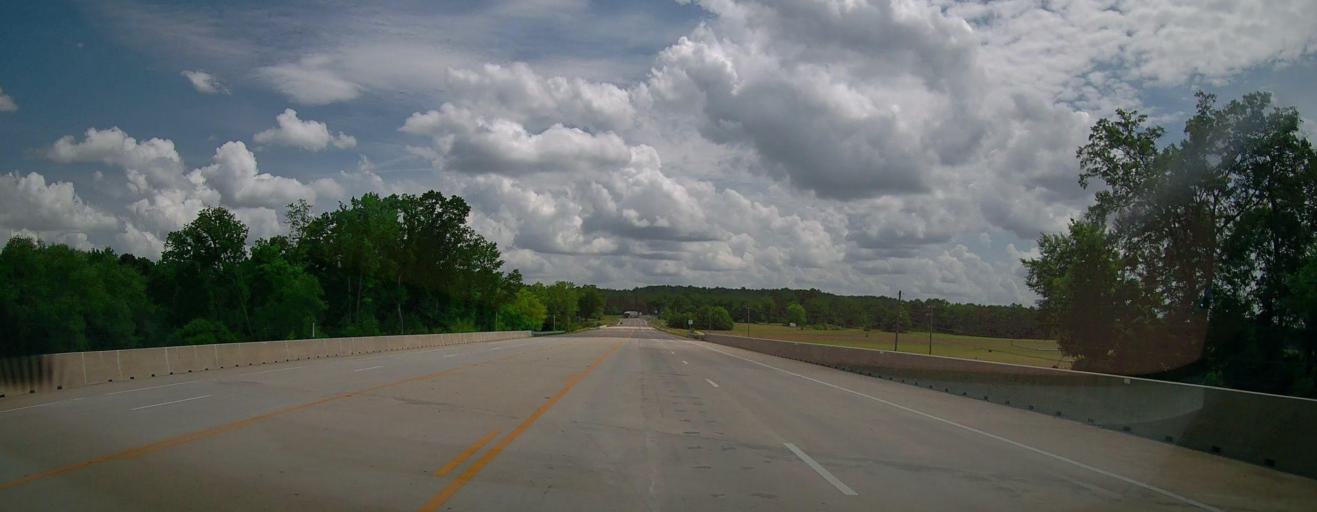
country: US
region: Alabama
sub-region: Marion County
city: Hamilton
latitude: 34.1065
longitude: -87.9892
